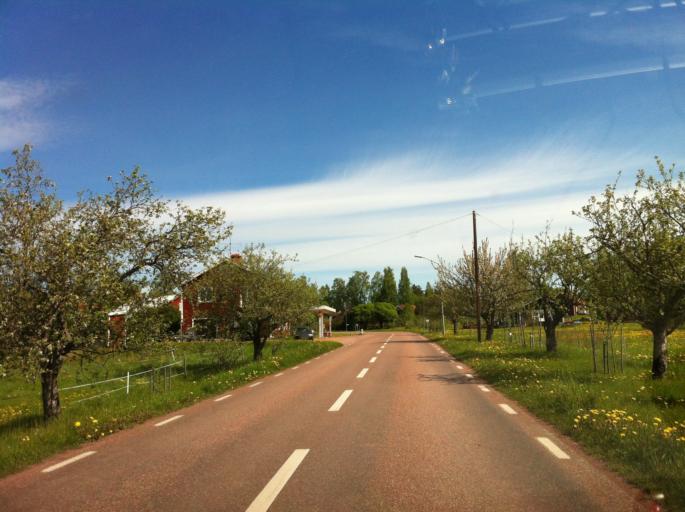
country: SE
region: Dalarna
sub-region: Mora Kommun
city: Mora
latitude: 60.9104
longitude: 14.6154
